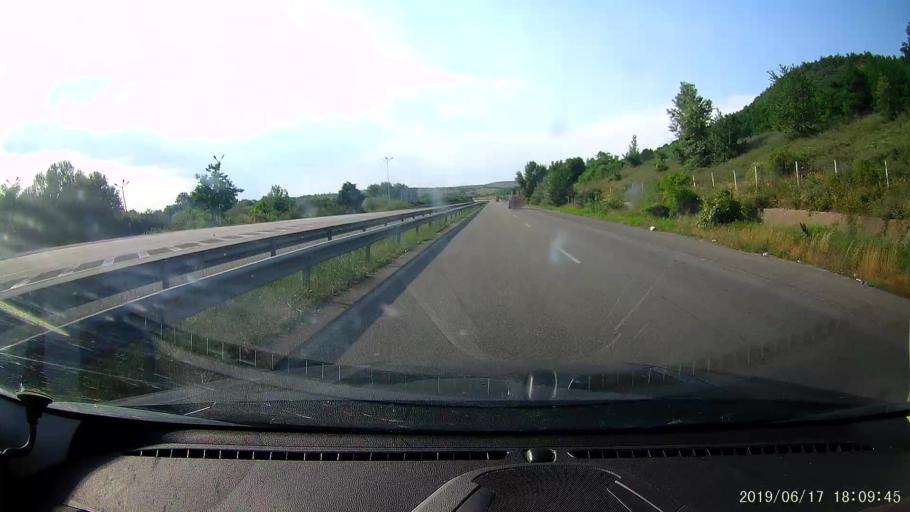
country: BG
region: Khaskovo
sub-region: Obshtina Lyubimets
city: Lyubimets
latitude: 41.8644
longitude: 26.0866
